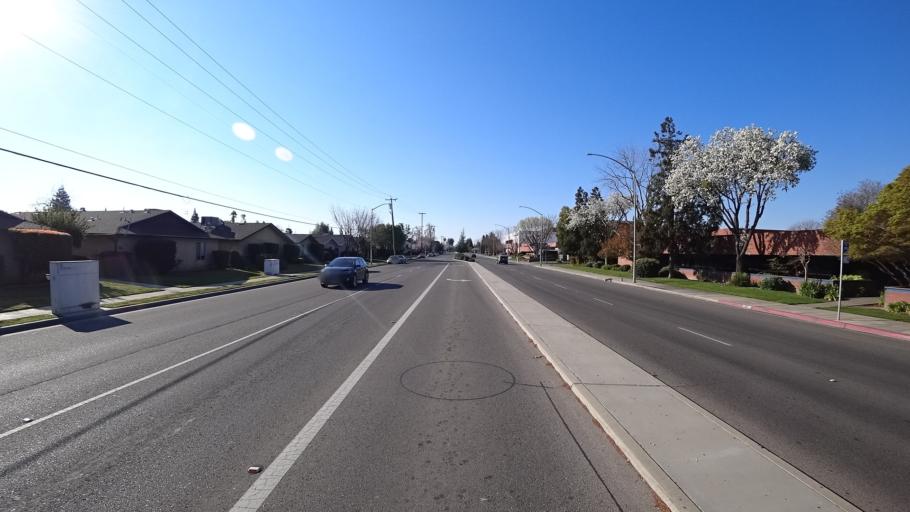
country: US
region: California
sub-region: Fresno County
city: Clovis
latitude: 36.8264
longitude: -119.7813
